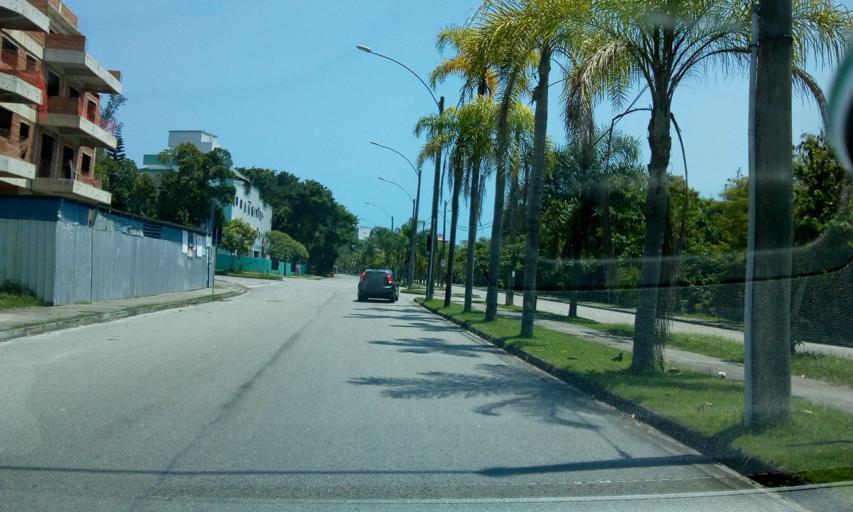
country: BR
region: Rio de Janeiro
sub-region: Nilopolis
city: Nilopolis
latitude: -23.0259
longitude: -43.4674
